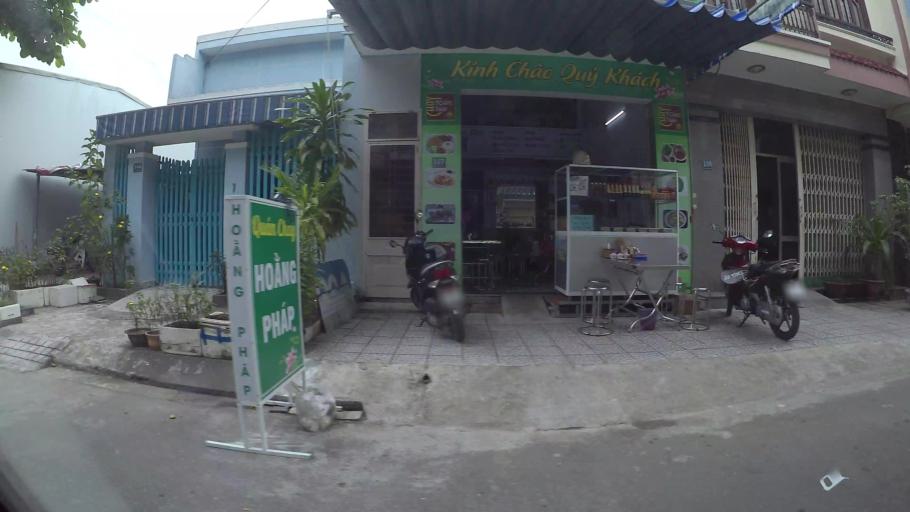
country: VN
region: Da Nang
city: Lien Chieu
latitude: 16.0781
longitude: 108.1653
